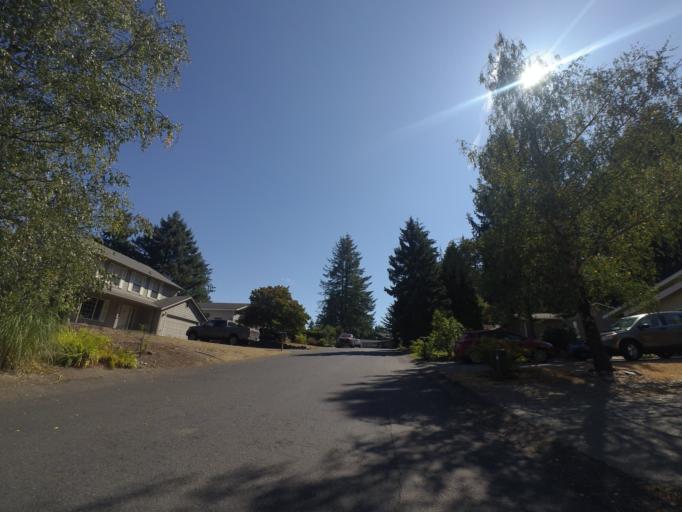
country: US
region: Washington
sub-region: Pierce County
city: Fircrest
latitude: 47.2150
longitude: -122.5172
